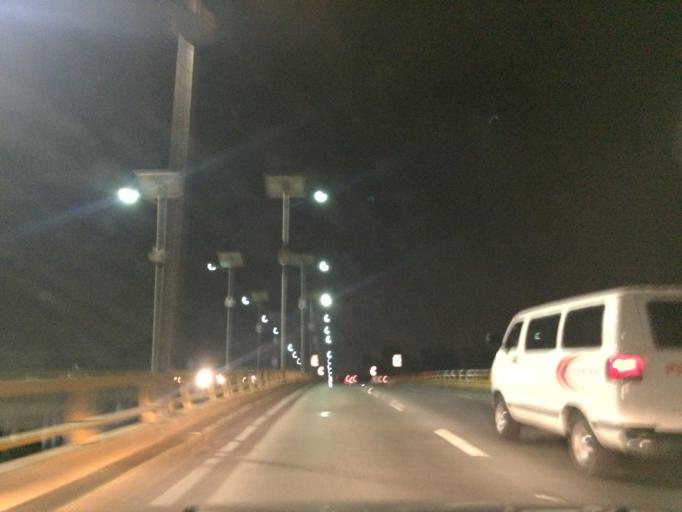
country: MX
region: Mexico City
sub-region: Iztacalco
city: Iztacalco
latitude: 19.3969
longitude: -99.0989
